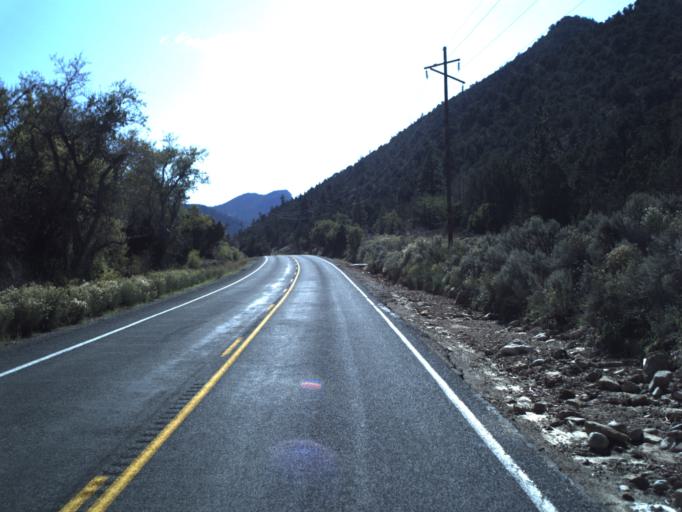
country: US
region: Utah
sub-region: Iron County
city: Parowan
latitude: 37.7900
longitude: -112.8230
